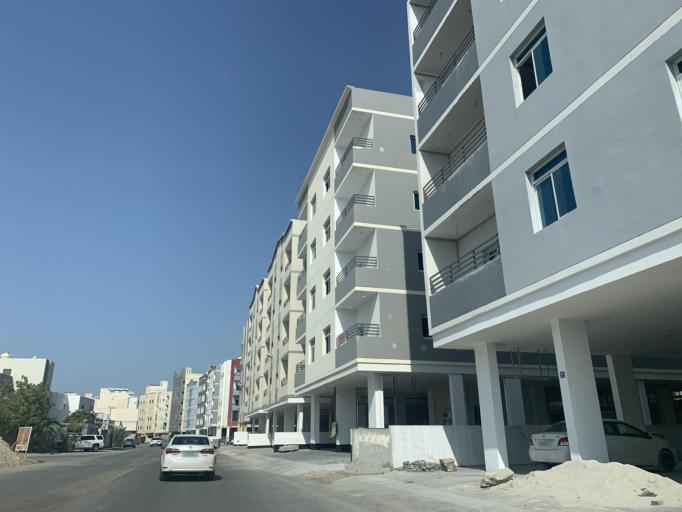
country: BH
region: Central Governorate
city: Madinat Hamad
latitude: 26.1334
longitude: 50.4881
